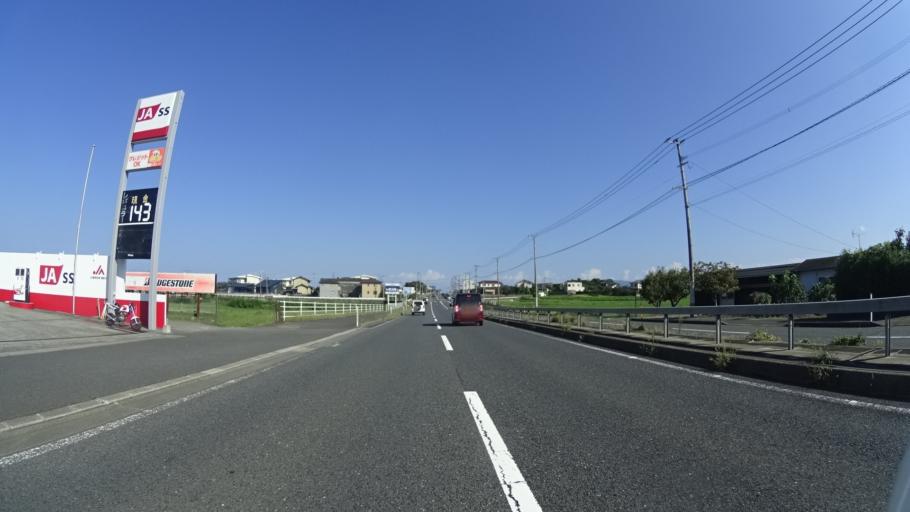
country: JP
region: Fukuoka
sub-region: Buzen-shi
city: Buzen
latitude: 33.6046
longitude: 131.1205
